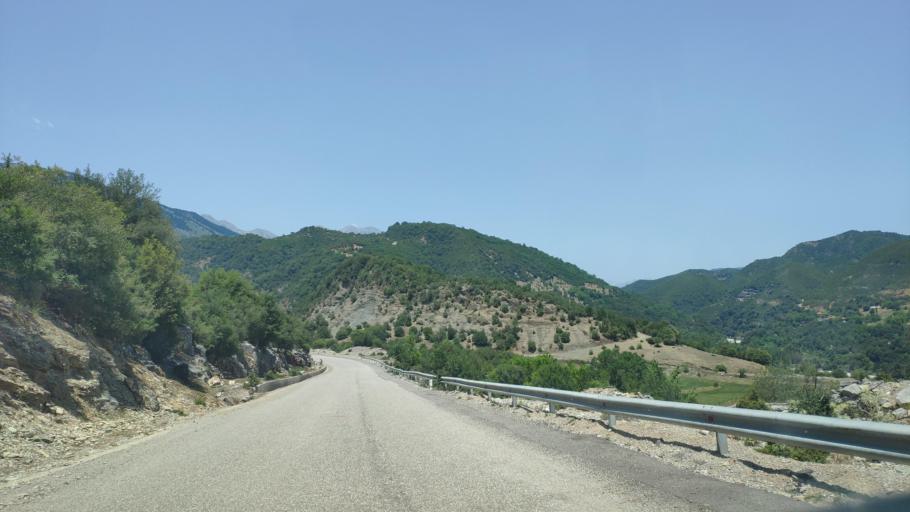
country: GR
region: Thessaly
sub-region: Nomos Kardhitsas
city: Anthiro
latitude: 39.1631
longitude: 21.3779
